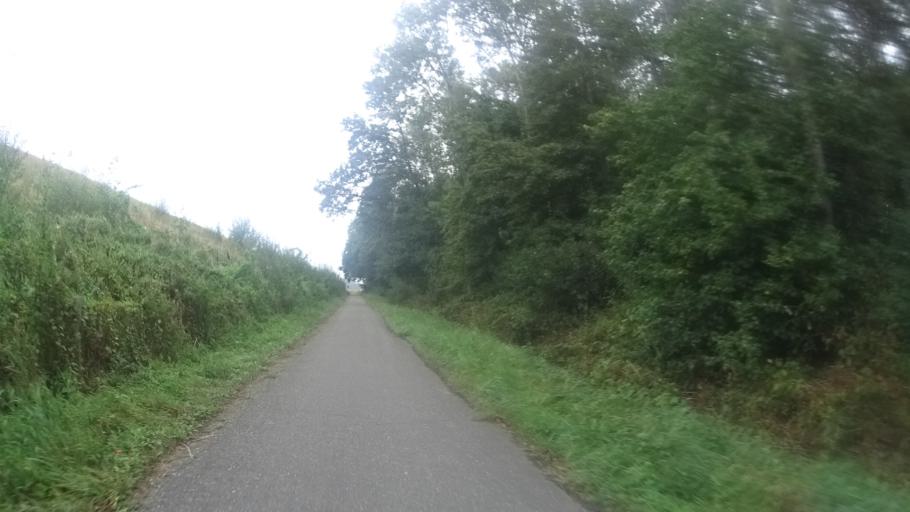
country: NL
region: Limburg
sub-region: Gemeente Venlo
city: Arcen
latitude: 51.4414
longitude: 6.1653
